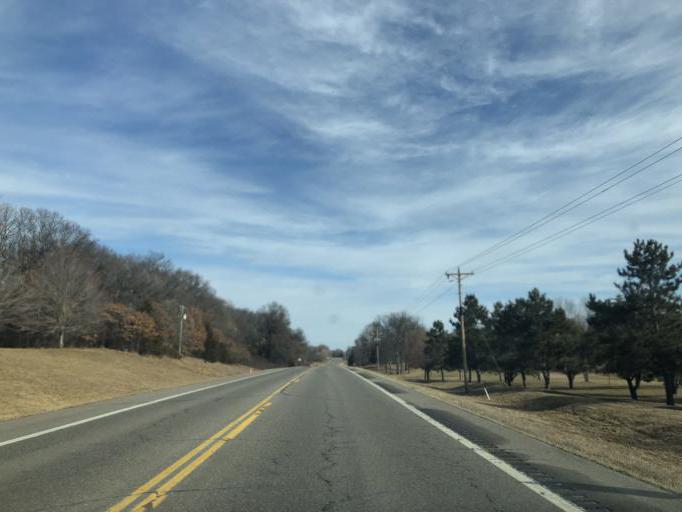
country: US
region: Minnesota
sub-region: Sherburne County
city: Becker
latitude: 45.4099
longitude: -93.8707
